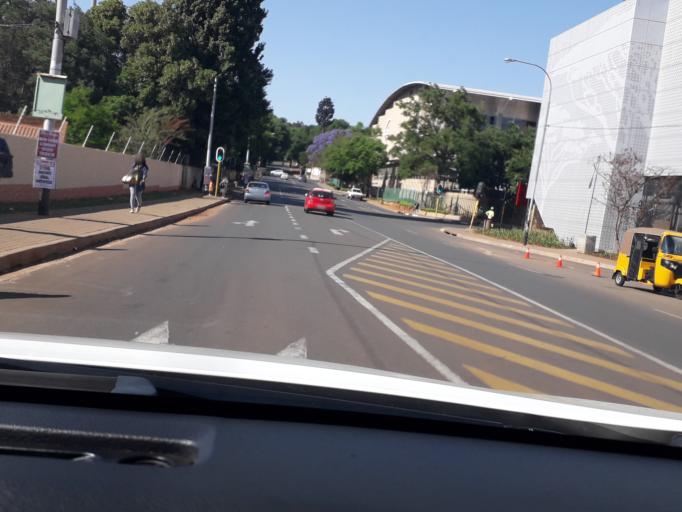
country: ZA
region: Gauteng
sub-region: City of Johannesburg Metropolitan Municipality
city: Johannesburg
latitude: -26.1817
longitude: 28.0068
